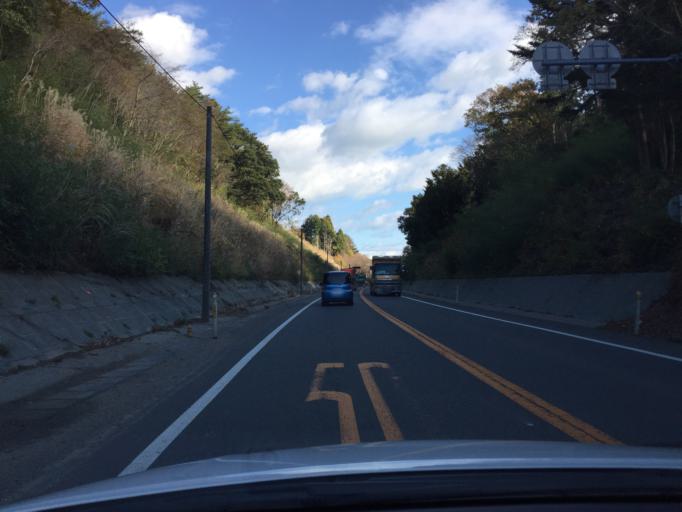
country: JP
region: Fukushima
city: Namie
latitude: 37.3169
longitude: 141.0017
